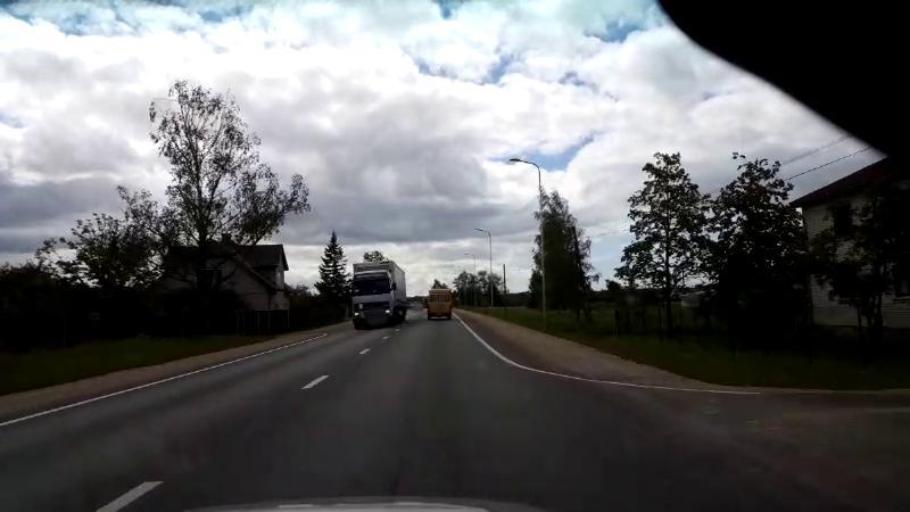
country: LV
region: Salacgrivas
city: Salacgriva
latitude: 57.7451
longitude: 24.3593
